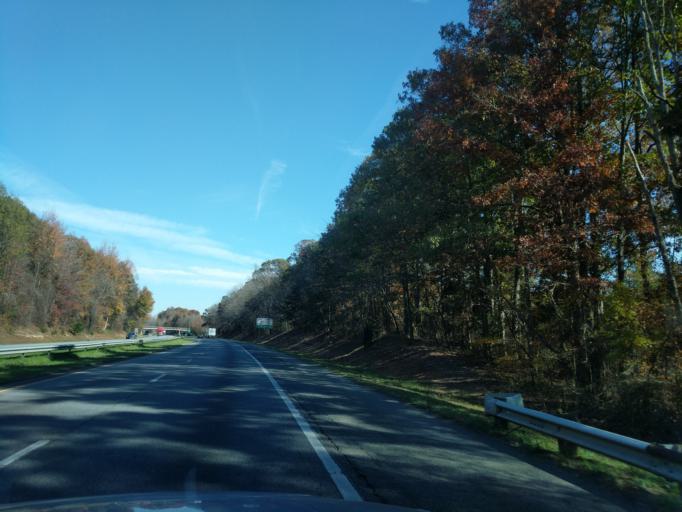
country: US
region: North Carolina
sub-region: Cleveland County
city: Kings Mountain
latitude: 35.2323
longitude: -81.3216
